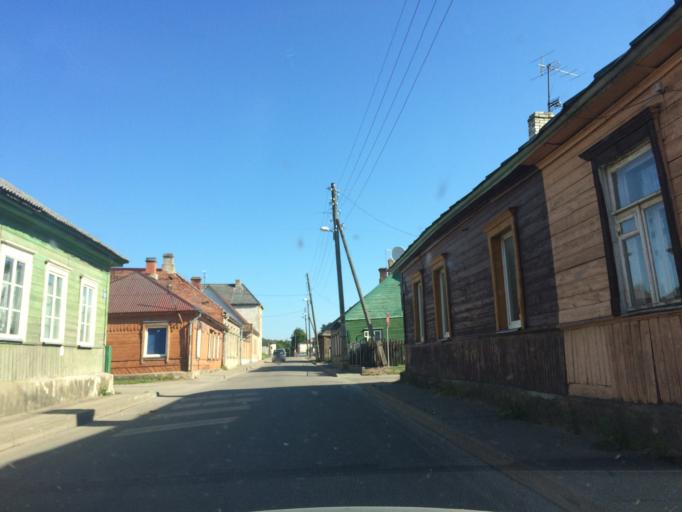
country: LV
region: Rezekne
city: Rezekne
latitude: 56.4979
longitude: 27.3353
